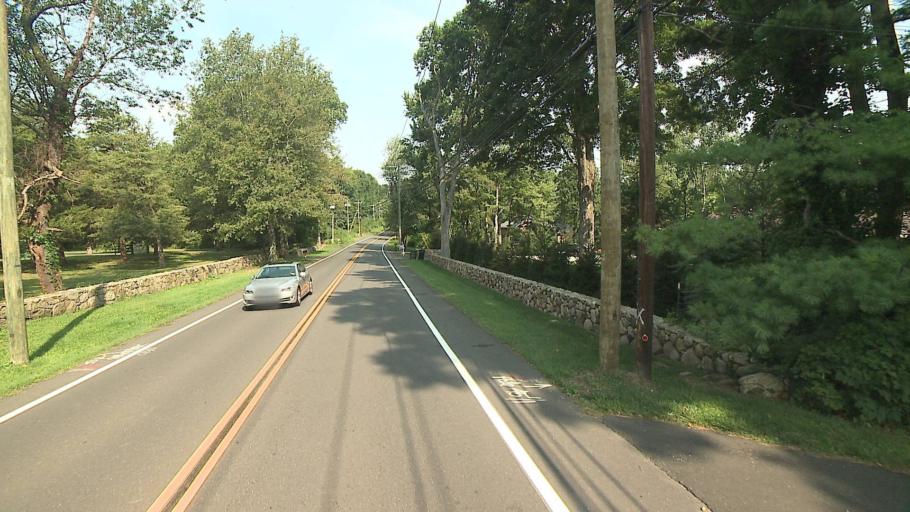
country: US
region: Connecticut
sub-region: Fairfield County
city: Georgetown
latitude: 41.2248
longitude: -73.3982
